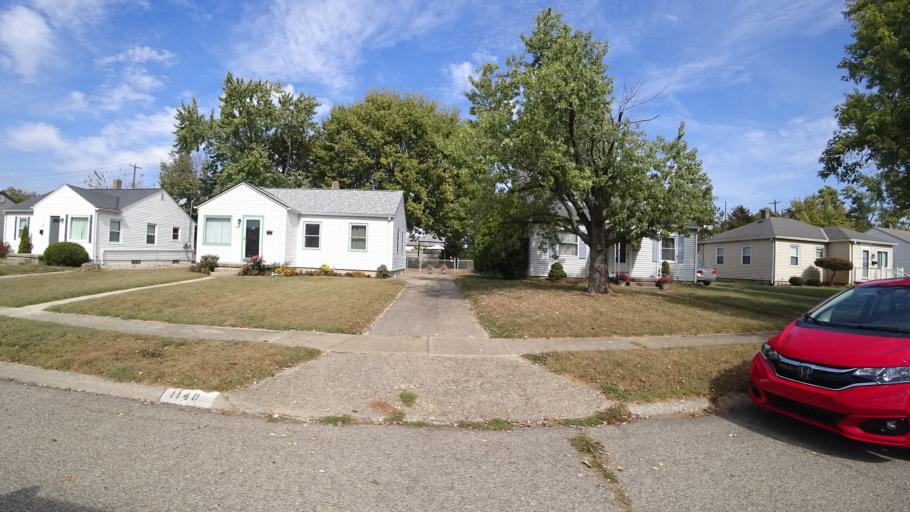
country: US
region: Ohio
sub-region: Butler County
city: Fairfield
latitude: 39.3605
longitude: -84.5457
